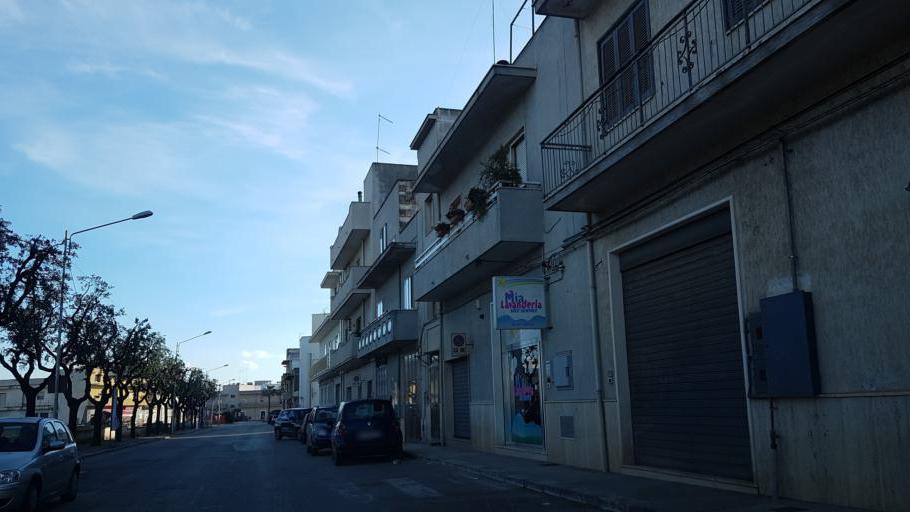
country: IT
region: Apulia
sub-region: Provincia di Brindisi
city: Carovigno
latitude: 40.7056
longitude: 17.6635
